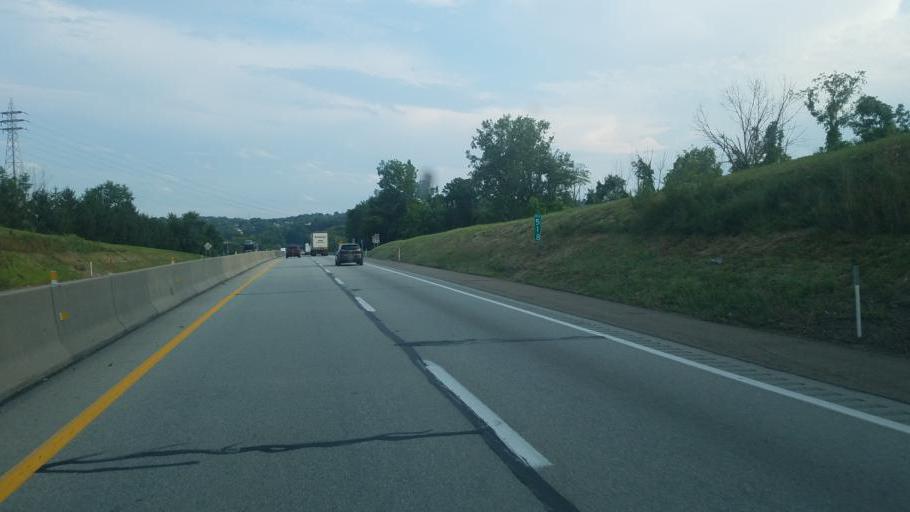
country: US
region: Pennsylvania
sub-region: Allegheny County
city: Plum
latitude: 40.4985
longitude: -79.7850
